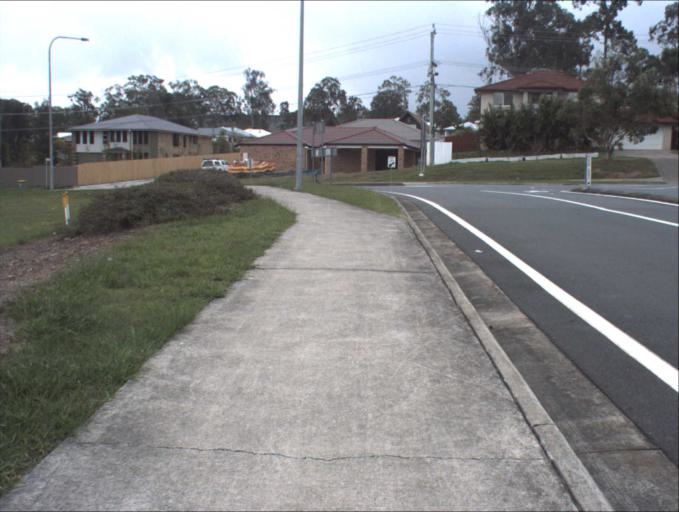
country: AU
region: Queensland
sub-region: Logan
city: Park Ridge South
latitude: -27.6807
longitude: 153.0296
